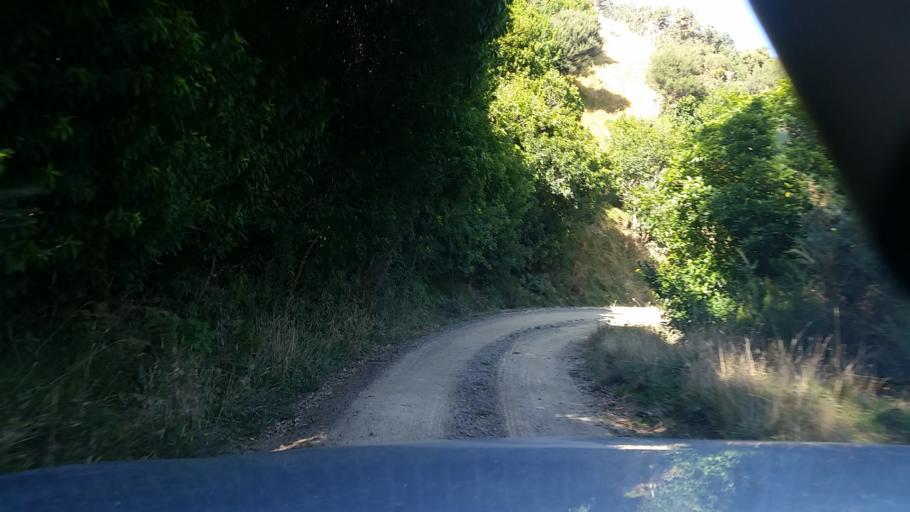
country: NZ
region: Marlborough
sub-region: Marlborough District
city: Picton
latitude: -41.3001
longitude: 174.1792
